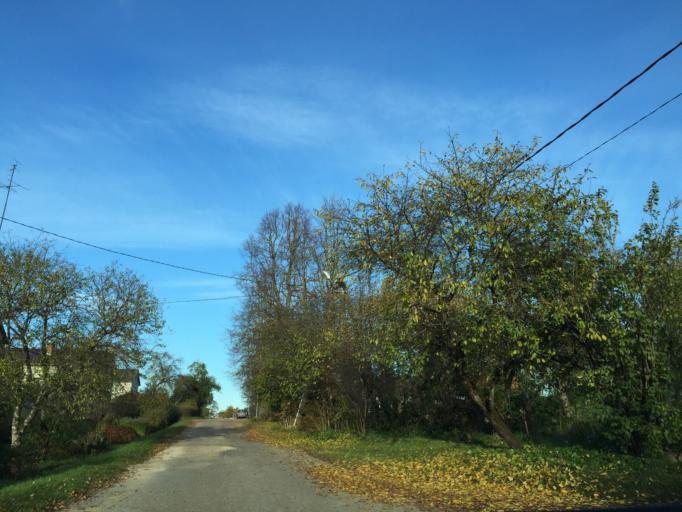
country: LV
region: Skriveri
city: Skriveri
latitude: 56.6250
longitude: 25.1276
